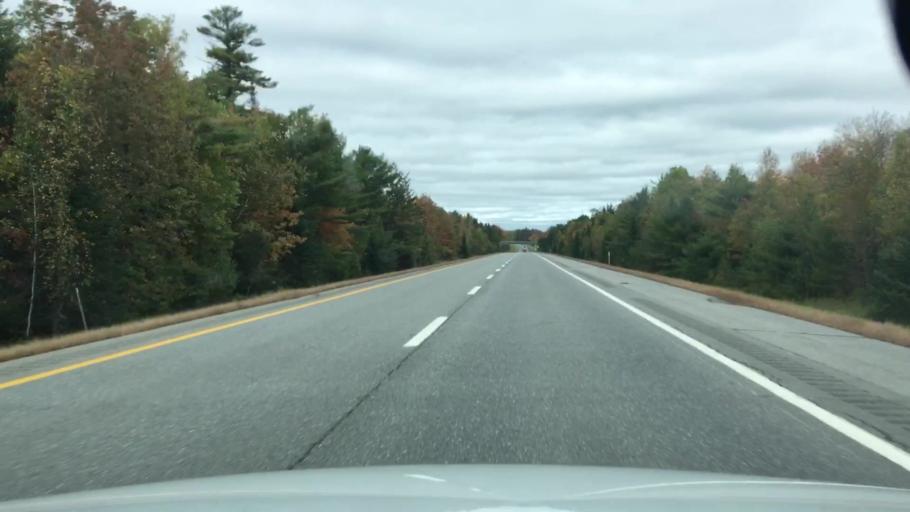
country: US
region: Maine
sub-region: Waldo County
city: Burnham
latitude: 44.7005
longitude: -69.4602
